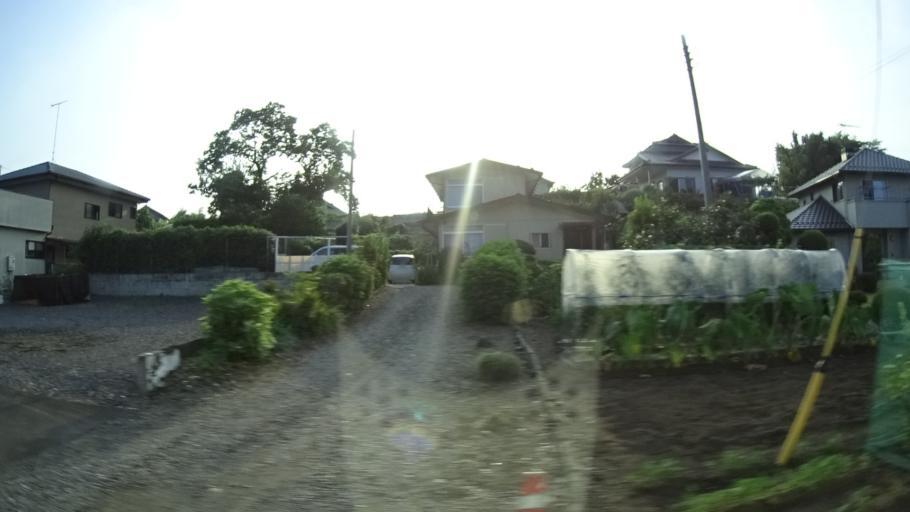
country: JP
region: Tochigi
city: Karasuyama
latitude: 36.6240
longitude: 140.1528
